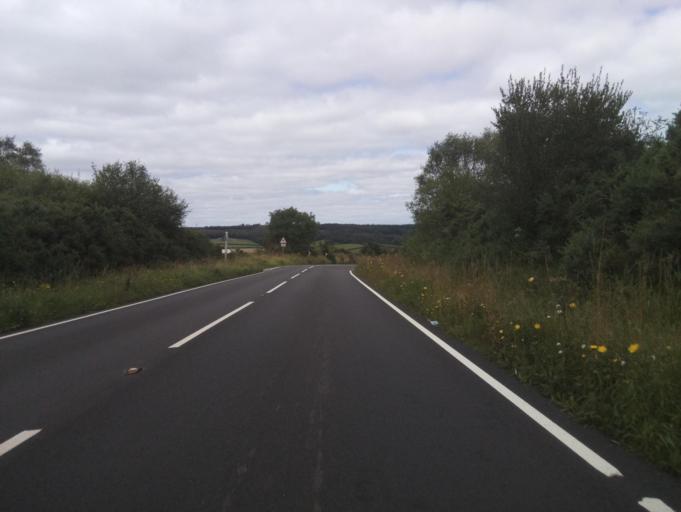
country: GB
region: England
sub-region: Devon
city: Bishopsteignton
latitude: 50.5812
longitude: -3.5317
